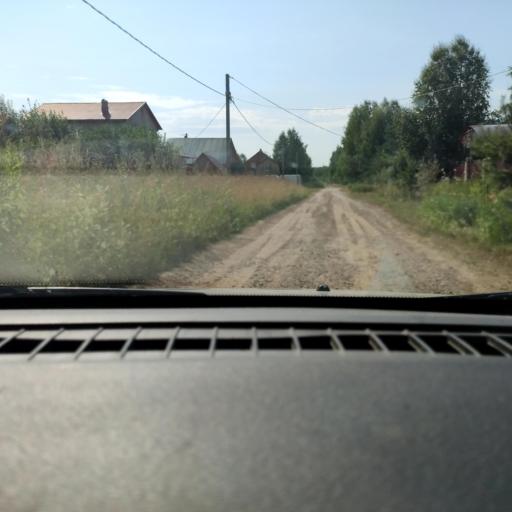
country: RU
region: Perm
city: Kondratovo
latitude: 58.0534
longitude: 56.0217
